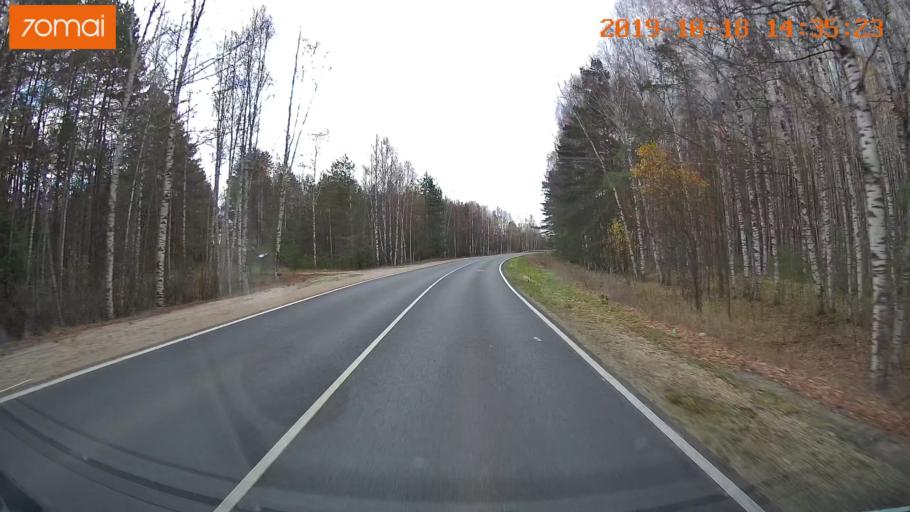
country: RU
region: Vladimir
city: Velikodvorskiy
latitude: 55.2224
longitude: 40.6360
